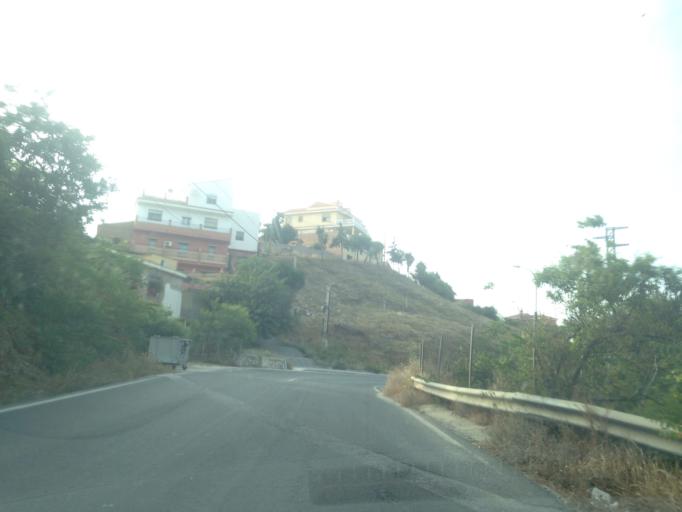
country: ES
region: Andalusia
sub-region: Provincia de Malaga
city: Malaga
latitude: 36.7406
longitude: -4.4123
